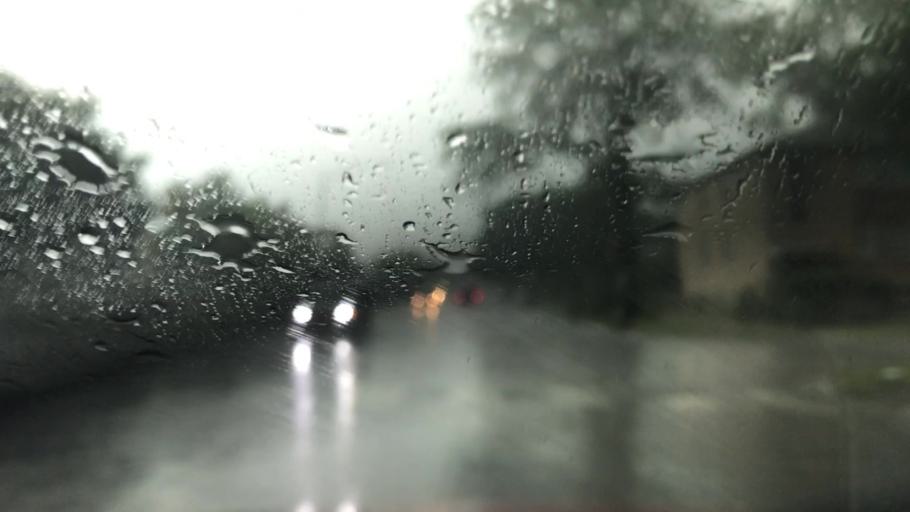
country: US
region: Illinois
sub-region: Cook County
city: Cicero
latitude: 41.8747
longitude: -87.7549
